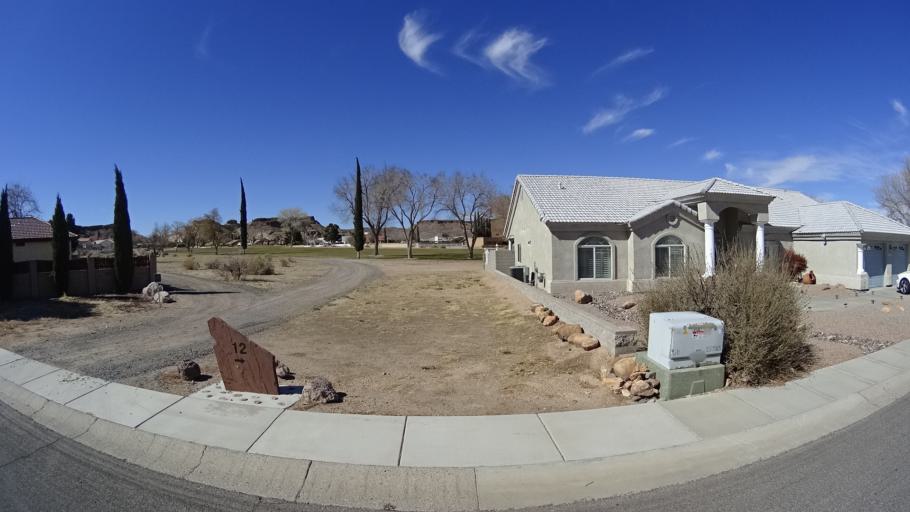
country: US
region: Arizona
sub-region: Mohave County
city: Kingman
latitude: 35.2114
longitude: -114.0457
